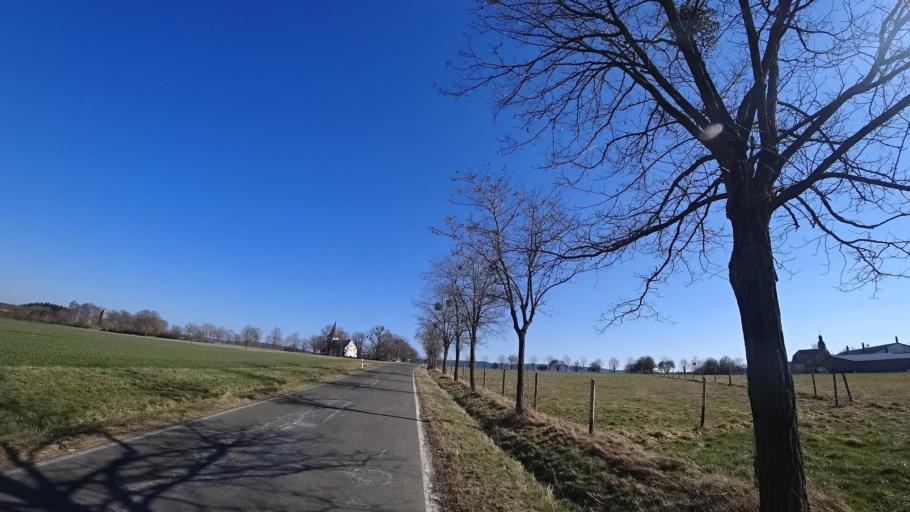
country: DE
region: Rheinland-Pfalz
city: Sargenroth
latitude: 49.9356
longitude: 7.5145
